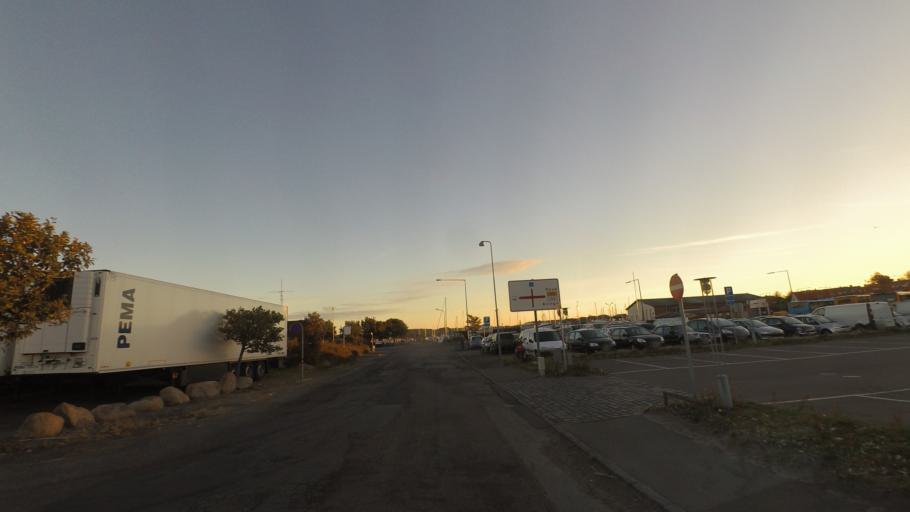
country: DK
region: Capital Region
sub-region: Bornholm Kommune
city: Ronne
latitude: 55.1025
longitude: 14.6907
